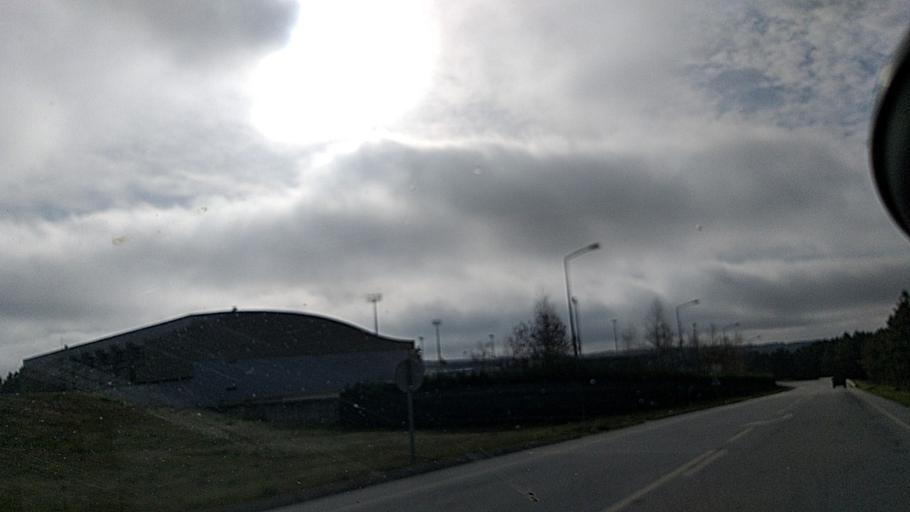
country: PT
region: Guarda
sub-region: Aguiar da Beira
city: Aguiar da Beira
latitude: 40.8150
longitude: -7.5369
